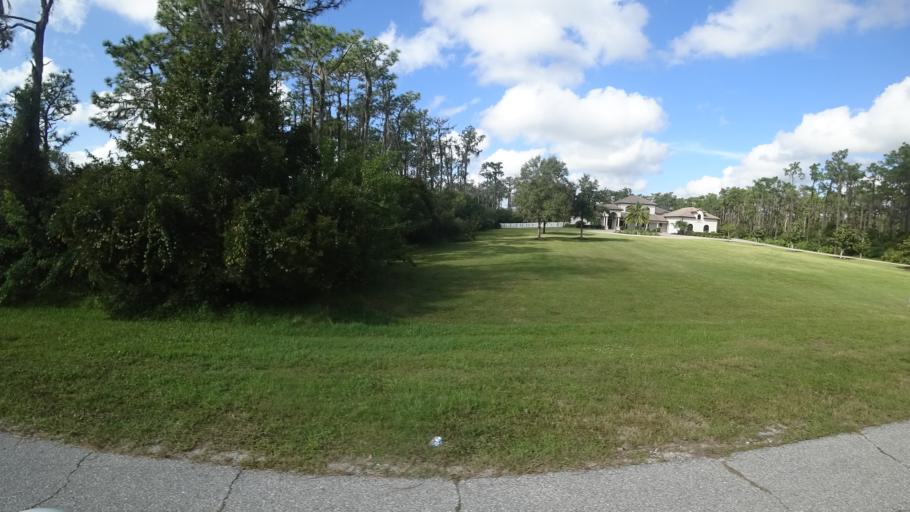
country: US
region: Florida
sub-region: Sarasota County
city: The Meadows
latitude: 27.4052
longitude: -82.3249
